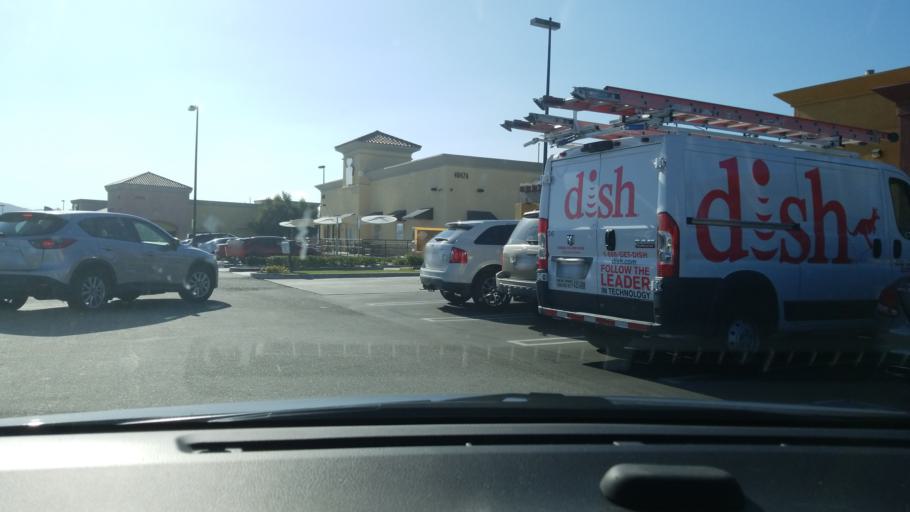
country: US
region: California
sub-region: Riverside County
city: Murrieta Hot Springs
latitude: 33.5555
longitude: -117.1788
